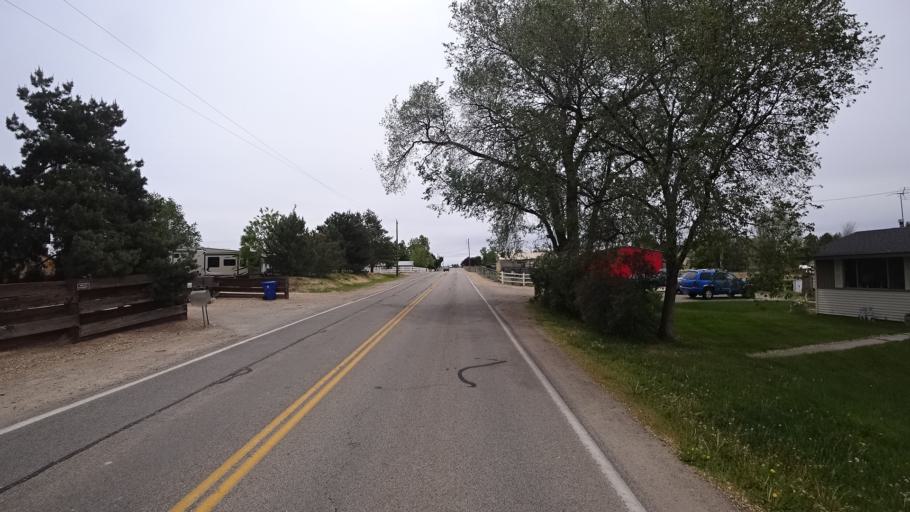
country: US
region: Idaho
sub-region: Ada County
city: Meridian
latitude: 43.5573
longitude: -116.3746
